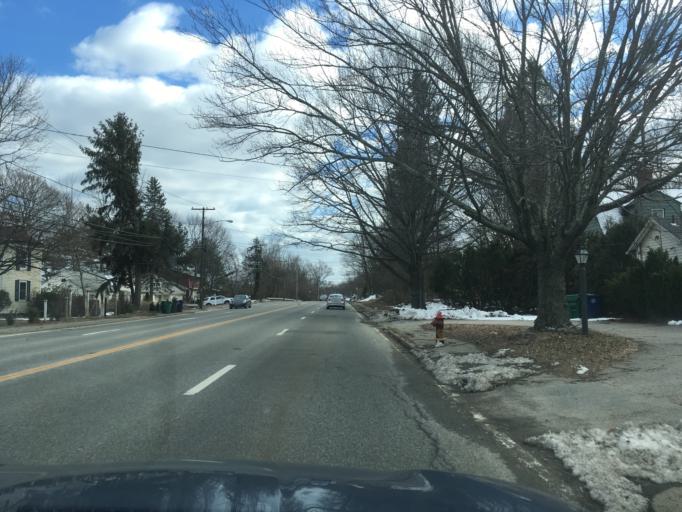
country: US
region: Rhode Island
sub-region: Kent County
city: East Greenwich
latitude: 41.7078
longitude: -71.4636
